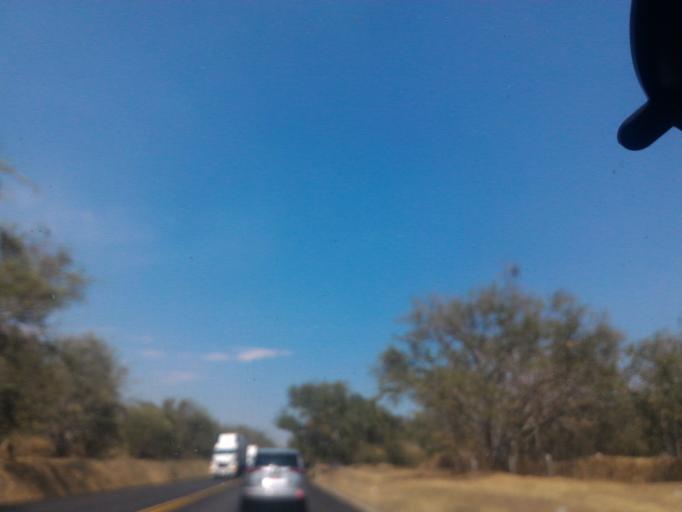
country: MX
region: Jalisco
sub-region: Tonila
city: San Marcos
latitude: 19.4725
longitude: -103.4623
